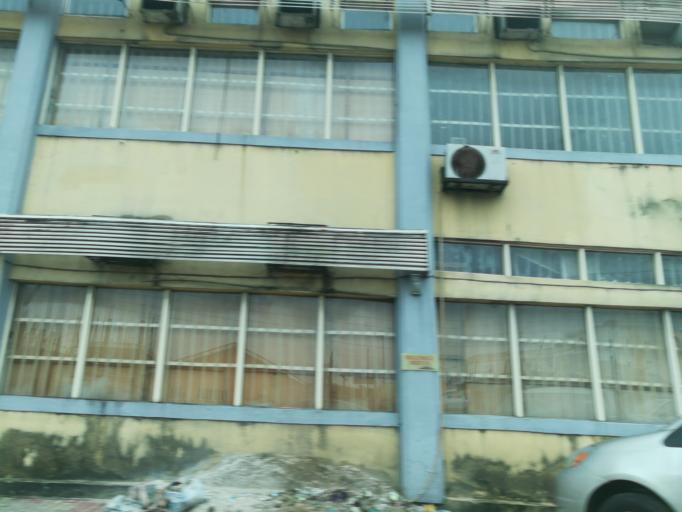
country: NG
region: Rivers
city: Port Harcourt
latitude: 4.8148
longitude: 6.9910
